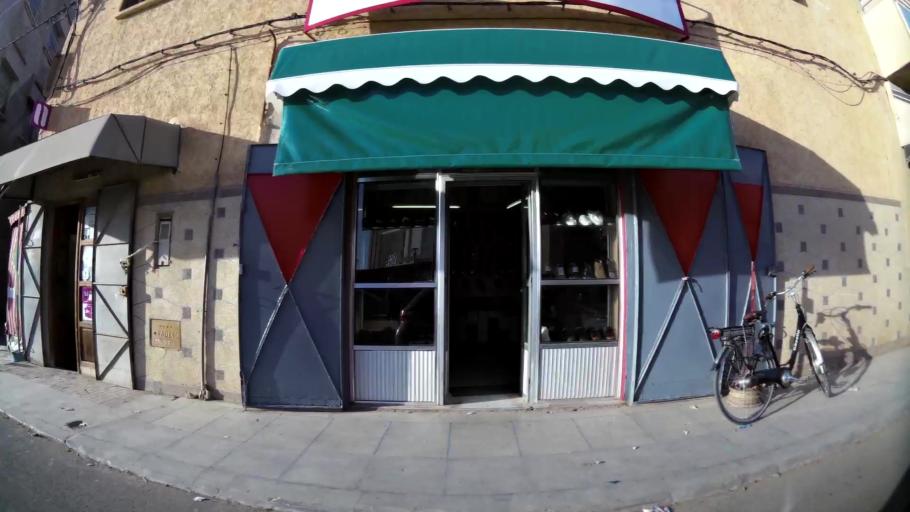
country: MA
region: Oriental
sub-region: Oujda-Angad
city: Oujda
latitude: 34.6792
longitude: -1.9059
